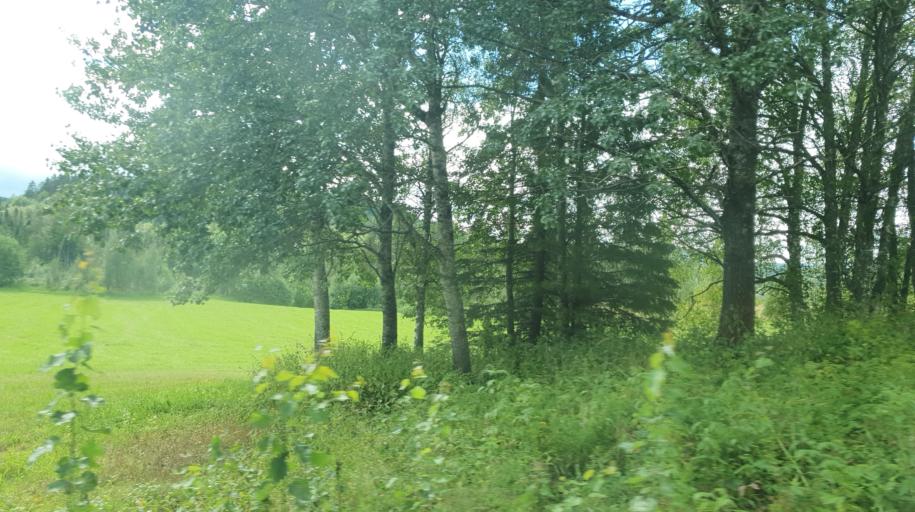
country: NO
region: Nord-Trondelag
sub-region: Levanger
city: Skogn
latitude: 63.6017
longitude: 11.2755
